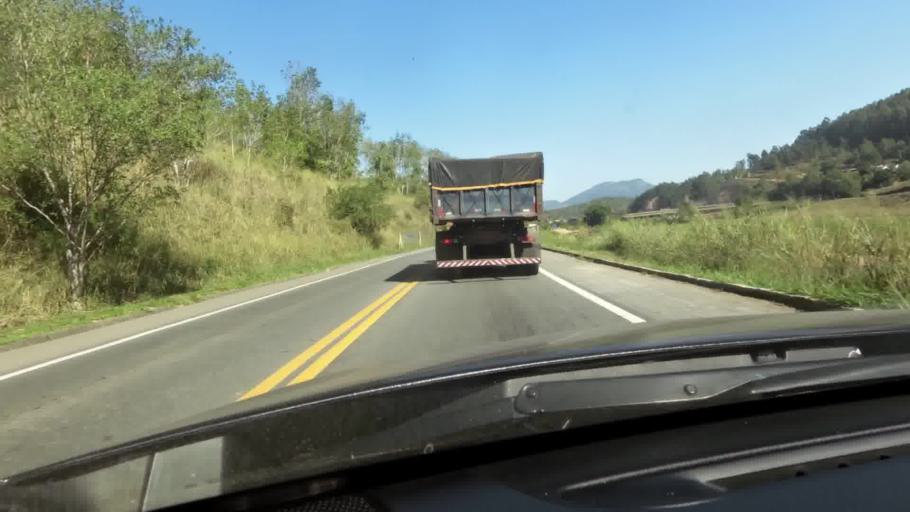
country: BR
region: Espirito Santo
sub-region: Cachoeiro De Itapemirim
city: Cachoeiro de Itapemirim
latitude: -20.8954
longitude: -41.0422
